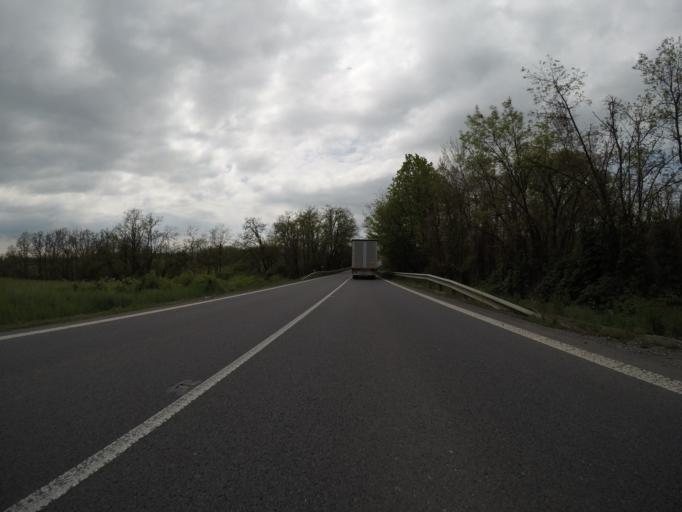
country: SK
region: Banskobystricky
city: Krupina
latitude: 48.3155
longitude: 19.0443
